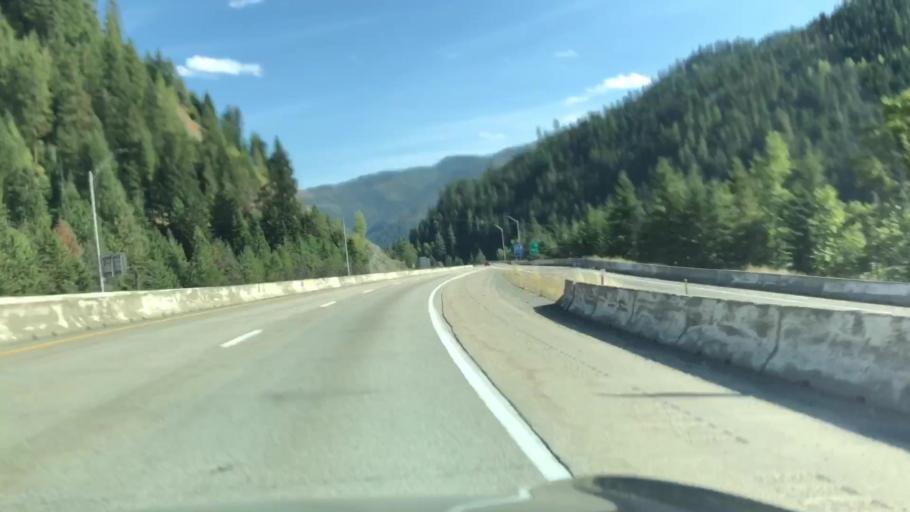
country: US
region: Idaho
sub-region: Shoshone County
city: Wallace
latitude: 47.4911
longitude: -115.9528
